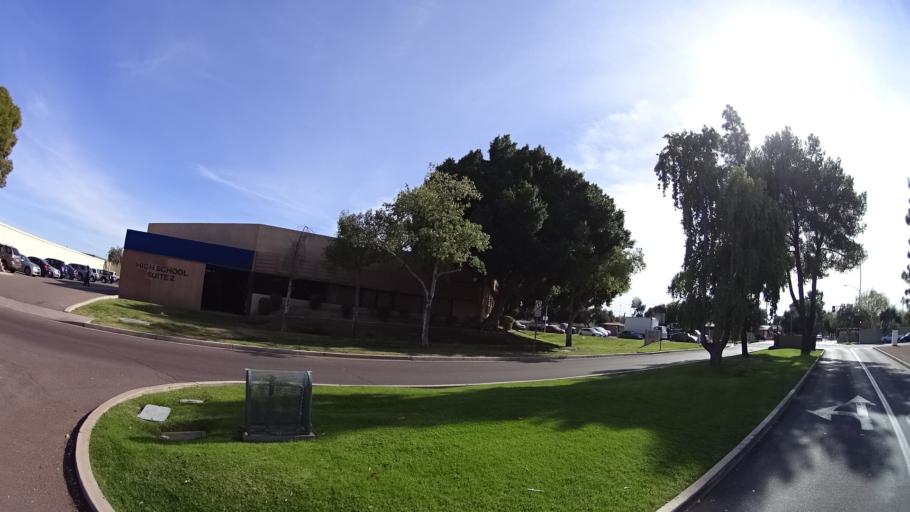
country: US
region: Arizona
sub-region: Maricopa County
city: Guadalupe
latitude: 33.3935
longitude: -111.9724
